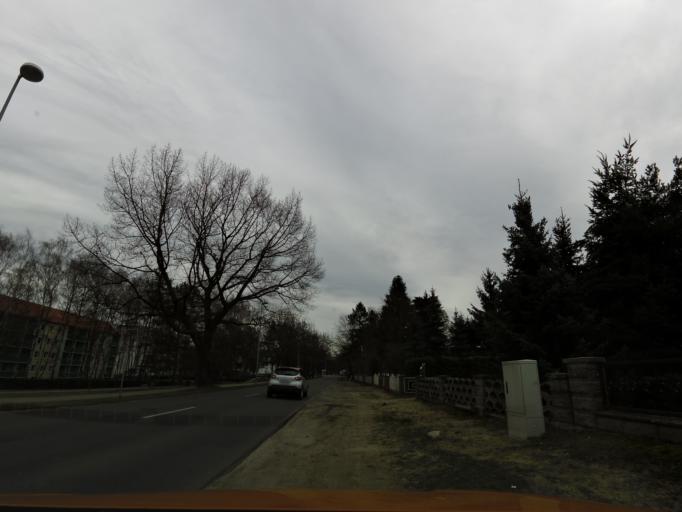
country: DE
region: Brandenburg
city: Belzig
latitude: 52.1388
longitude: 12.6018
